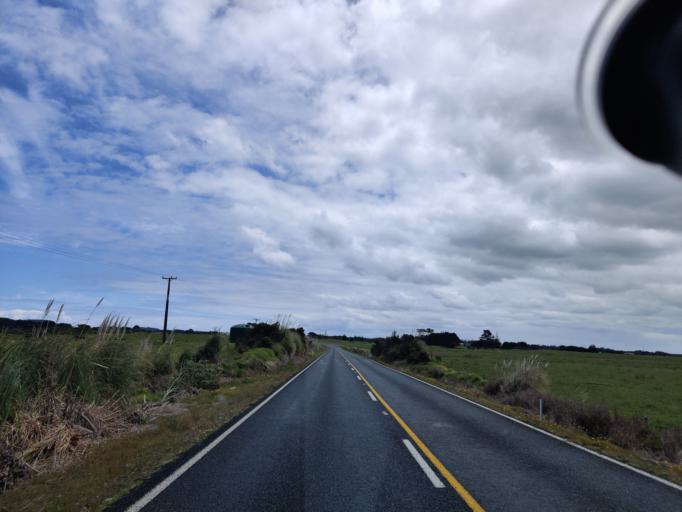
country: NZ
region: Northland
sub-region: Far North District
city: Kaitaia
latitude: -34.6767
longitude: 173.0022
